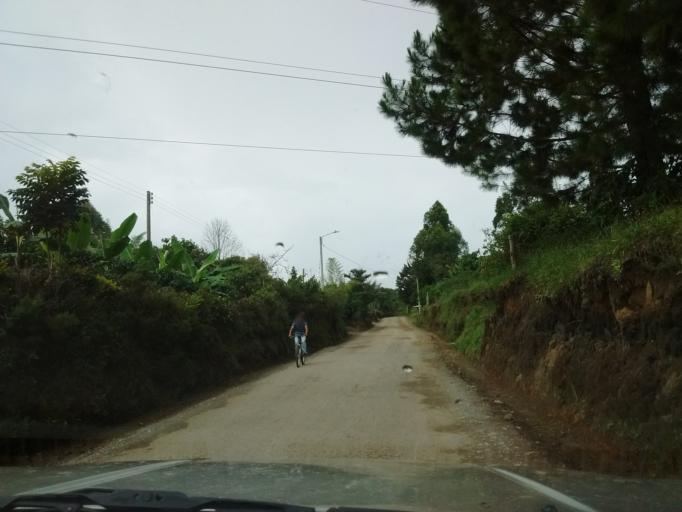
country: CO
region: Cauca
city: Popayan
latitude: 2.5263
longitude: -76.6011
